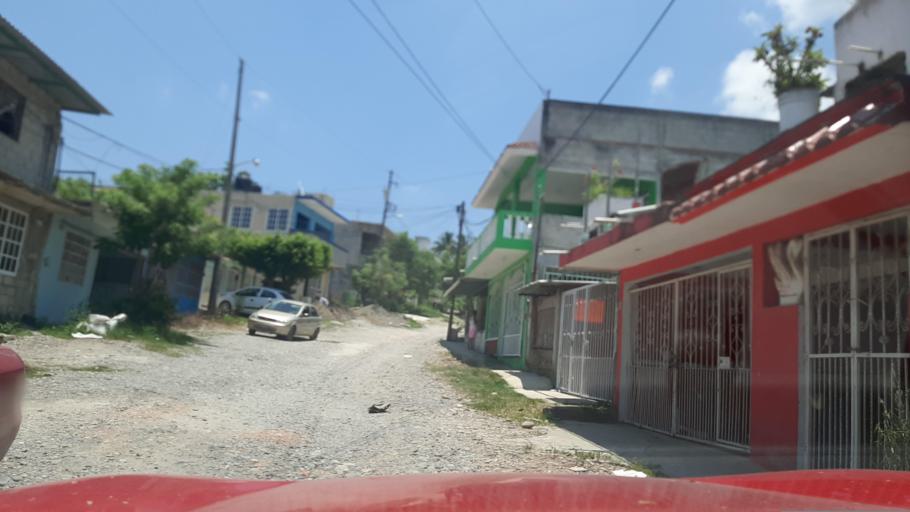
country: MX
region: Veracruz
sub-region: Poza Rica de Hidalgo
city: El Mollejon
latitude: 20.5406
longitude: -97.4115
